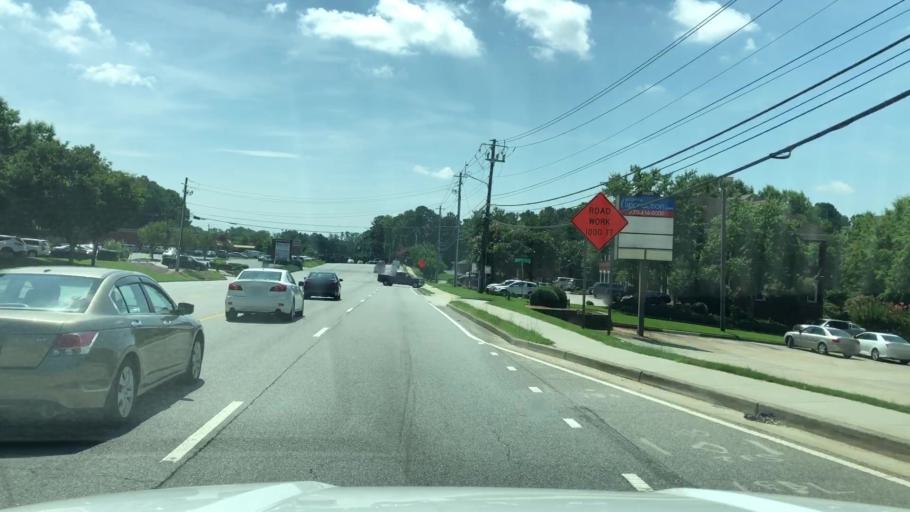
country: US
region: Georgia
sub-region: Gwinnett County
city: Norcross
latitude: 33.9552
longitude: -84.2446
